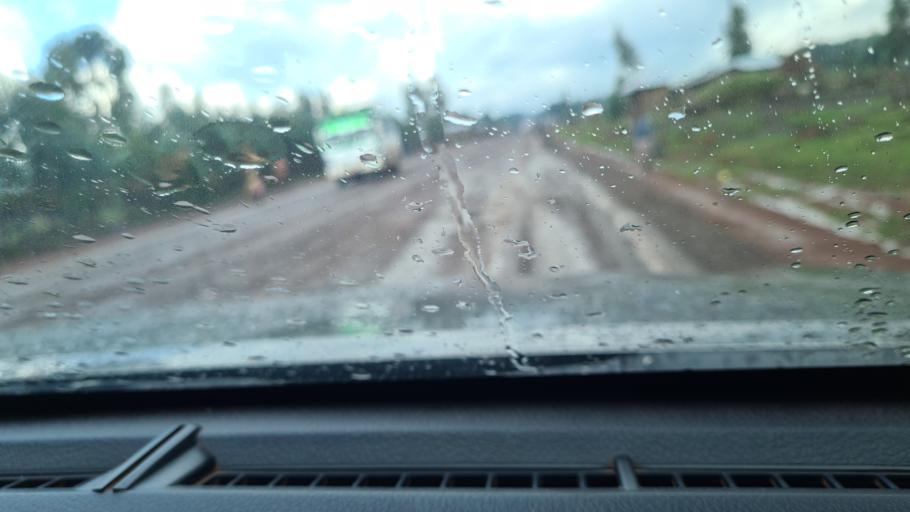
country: ET
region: Oromiya
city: Huruta
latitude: 8.0755
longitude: 39.5477
